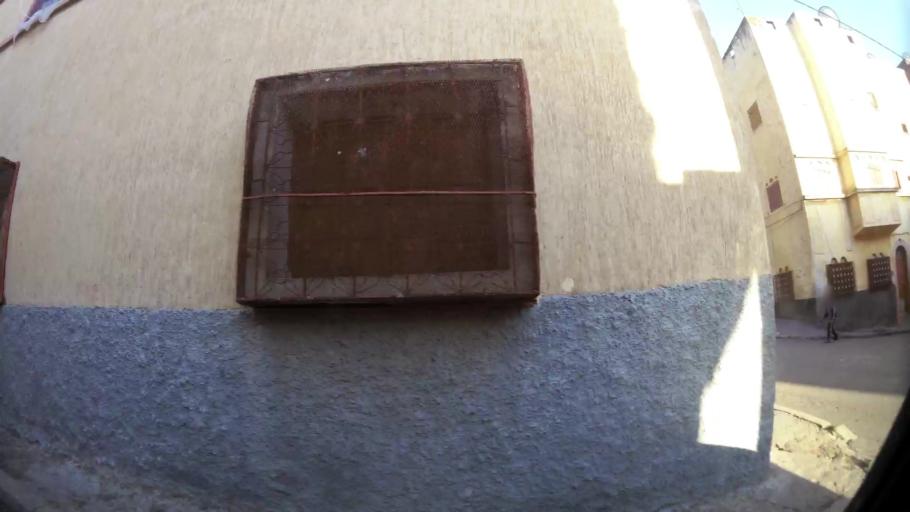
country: MA
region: Chaouia-Ouardigha
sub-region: Settat Province
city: Settat
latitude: 32.9995
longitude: -7.6076
